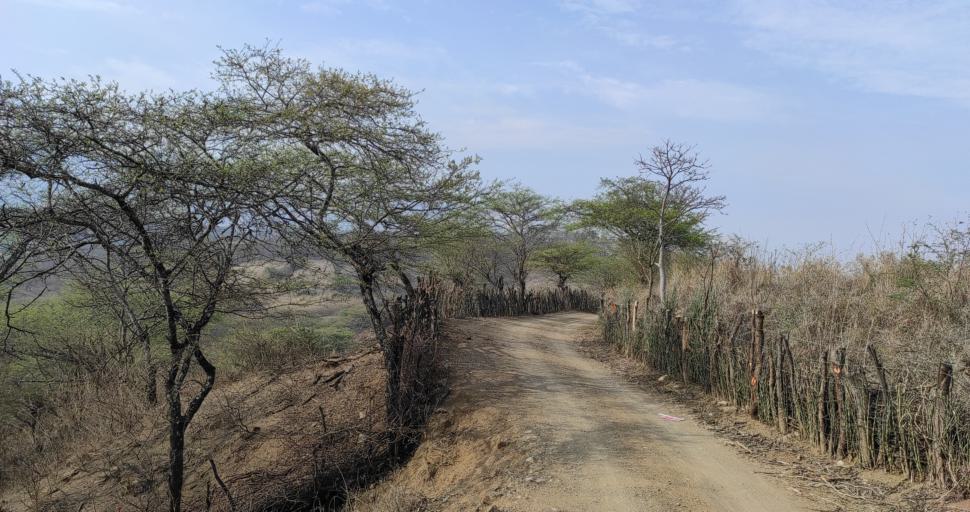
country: EC
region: Loja
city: Catacocha
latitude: -4.0089
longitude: -79.7001
